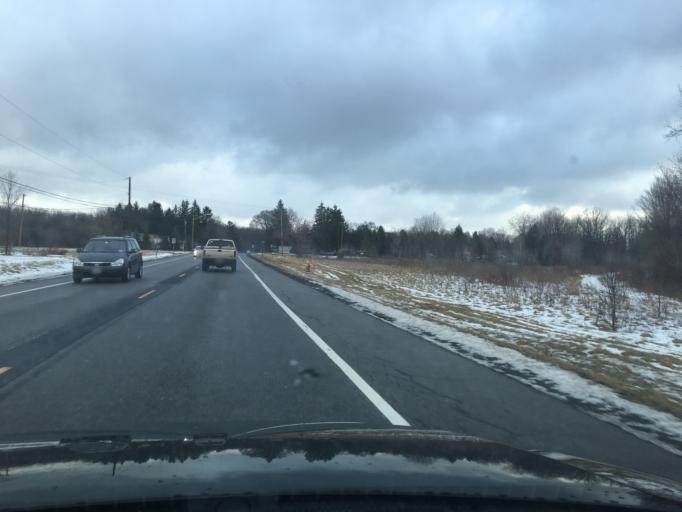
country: US
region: New York
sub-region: Ontario County
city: Manchester
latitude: 42.9730
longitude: -77.2418
